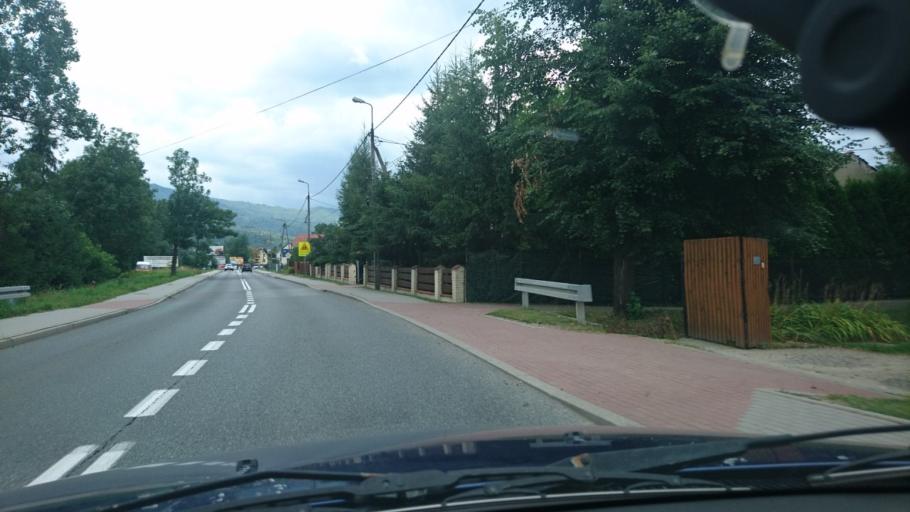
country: PL
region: Silesian Voivodeship
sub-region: Powiat zywiecki
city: Cisiec
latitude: 49.5790
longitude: 19.1016
